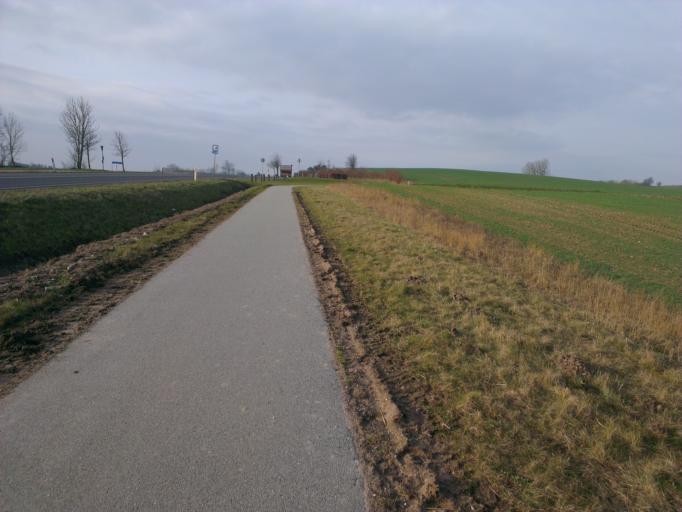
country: DK
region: Capital Region
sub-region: Frederikssund Kommune
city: Skibby
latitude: 55.7819
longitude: 11.9690
